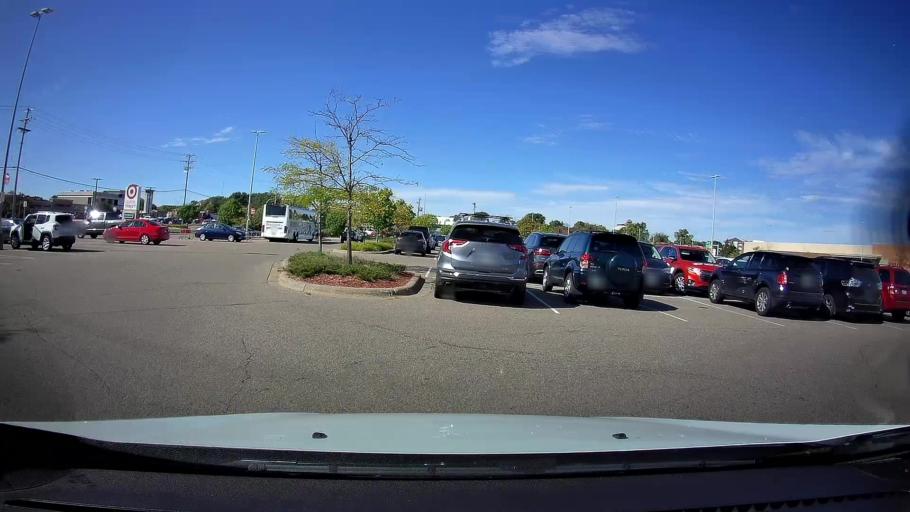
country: US
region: Minnesota
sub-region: Ramsey County
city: Roseville
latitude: 45.0067
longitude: -93.1633
